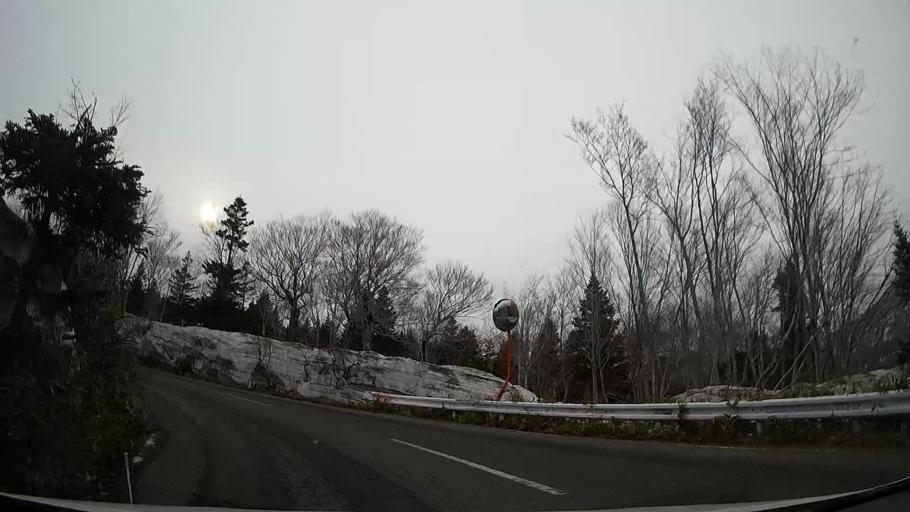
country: JP
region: Aomori
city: Aomori Shi
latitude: 40.6321
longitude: 140.9055
